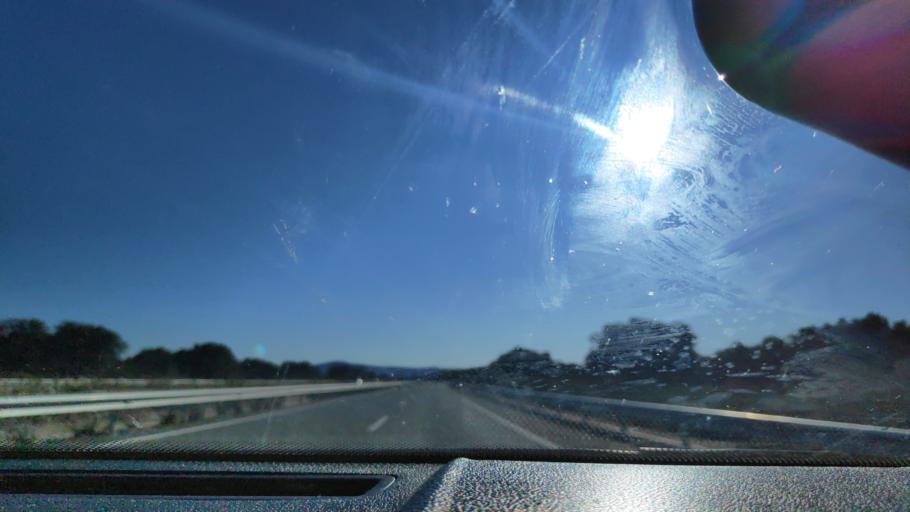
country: ES
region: Extremadura
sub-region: Provincia de Badajoz
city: Monesterio
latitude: 38.0161
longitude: -6.2263
